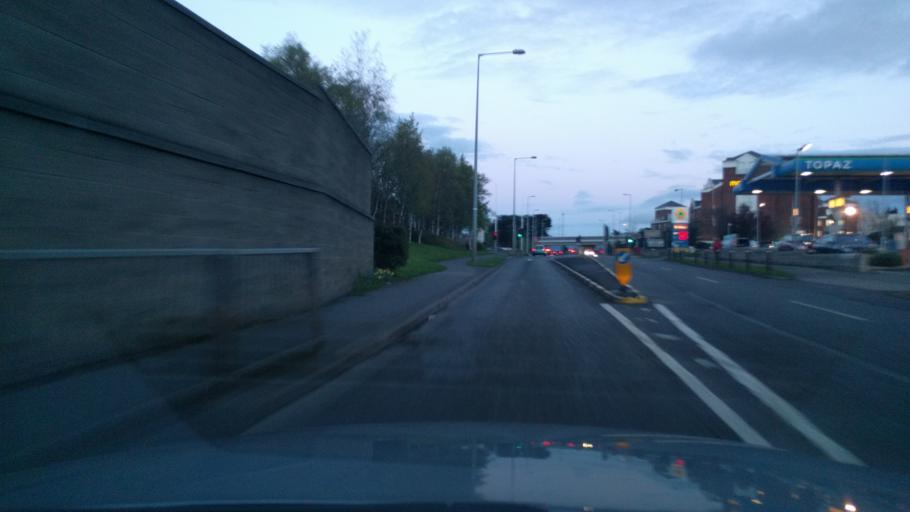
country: IE
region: Leinster
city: Clondalkin
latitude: 53.3151
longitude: -6.3943
